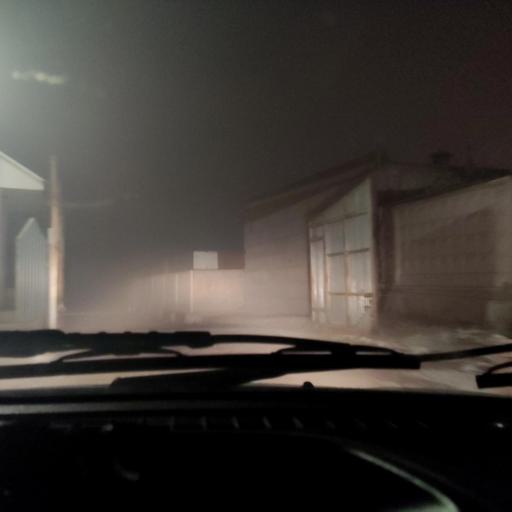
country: RU
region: Samara
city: Zhigulevsk
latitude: 53.4881
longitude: 49.4822
